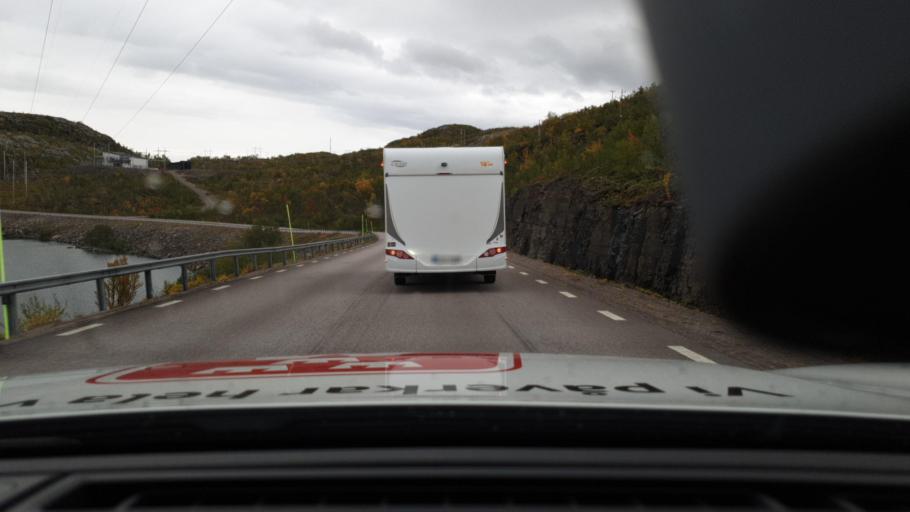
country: NO
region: Troms
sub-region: Bardu
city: Setermoen
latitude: 68.4337
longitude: 18.5789
